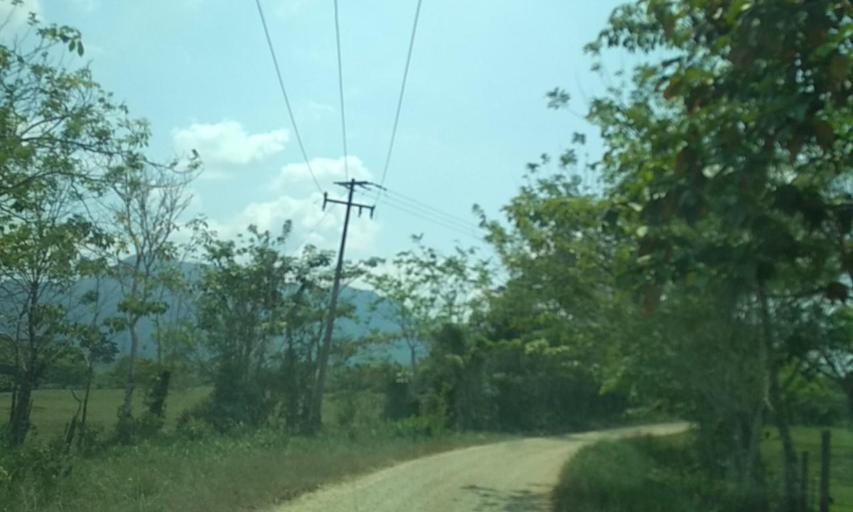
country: MX
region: Chiapas
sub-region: Tecpatan
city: Raudales Malpaso
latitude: 17.3443
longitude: -93.9607
